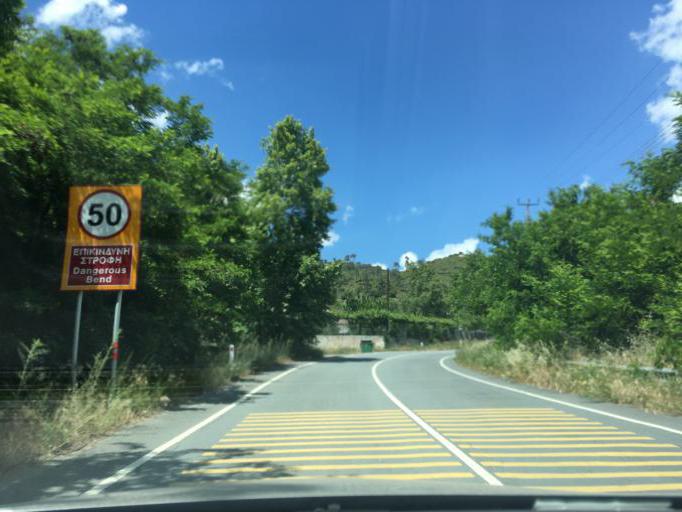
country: CY
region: Limassol
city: Pelendri
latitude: 34.8981
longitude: 32.9363
